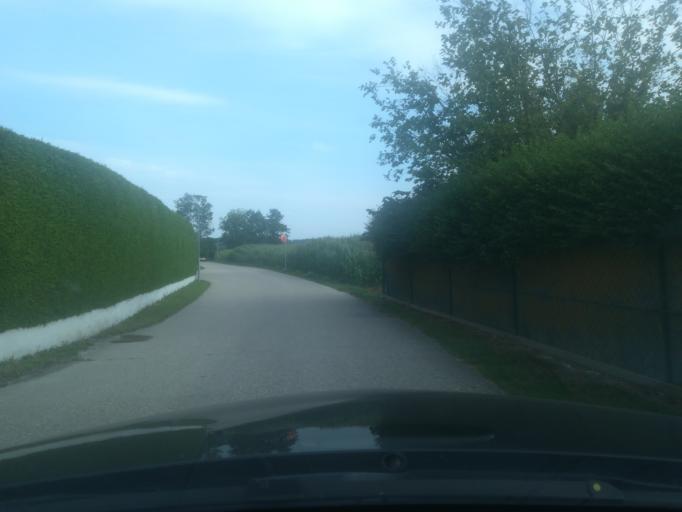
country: AT
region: Upper Austria
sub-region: Wels-Land
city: Marchtrenk
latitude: 48.1862
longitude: 14.1314
